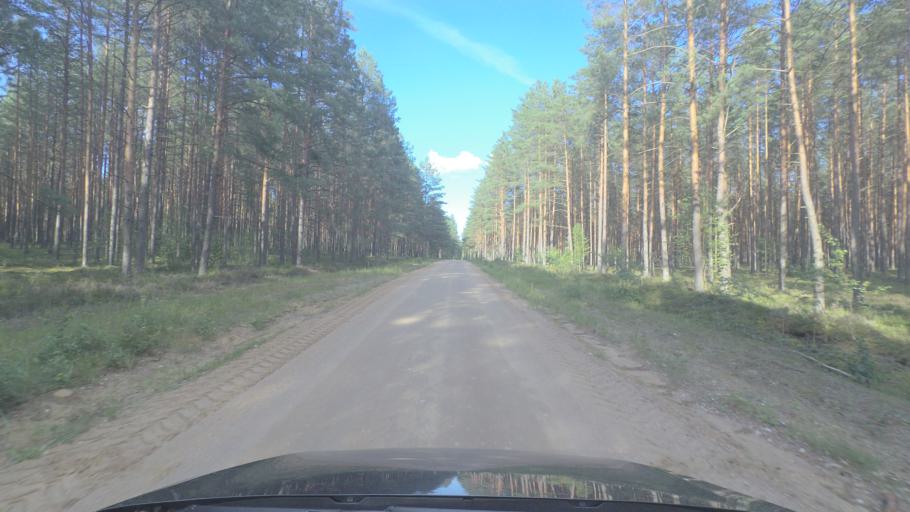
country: LT
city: Pabrade
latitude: 55.1596
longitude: 25.8097
